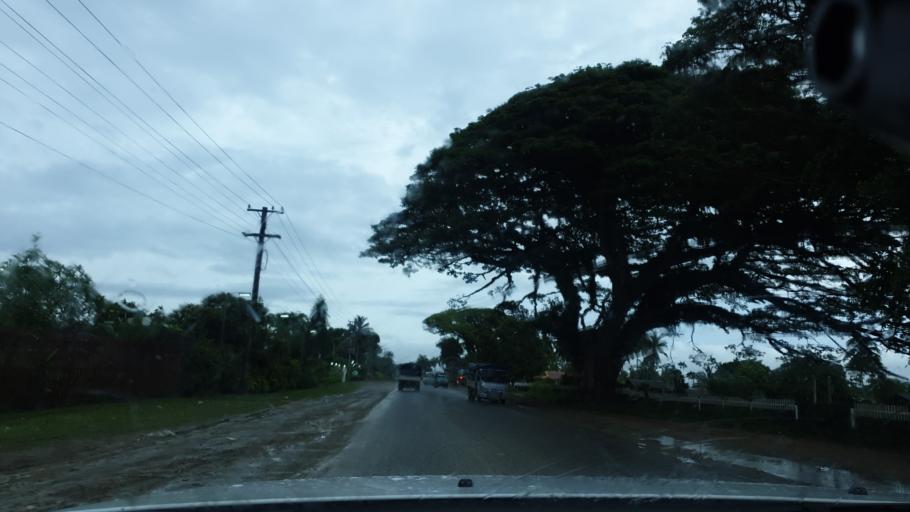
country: PG
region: Madang
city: Madang
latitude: -5.2289
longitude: 145.7975
